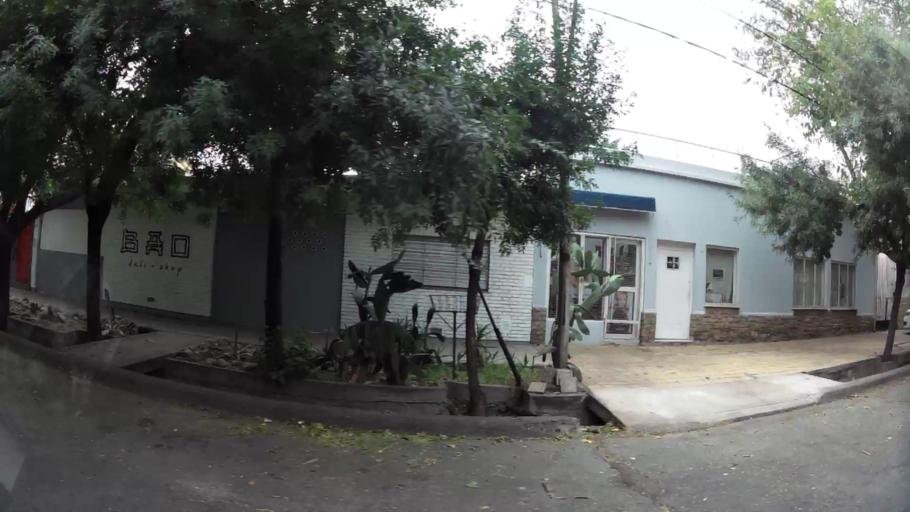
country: AR
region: Mendoza
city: Mendoza
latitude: -32.8854
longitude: -68.8531
